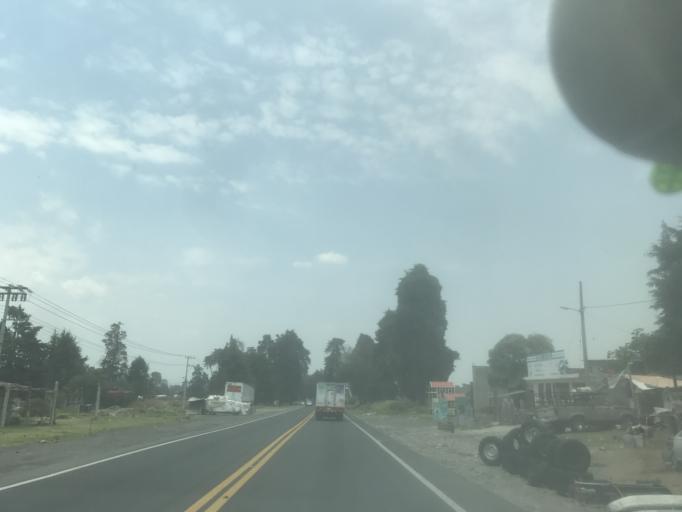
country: MX
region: Mexico
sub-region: Amecameca
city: San Diego Huehuecalco
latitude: 19.0835
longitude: -98.7820
